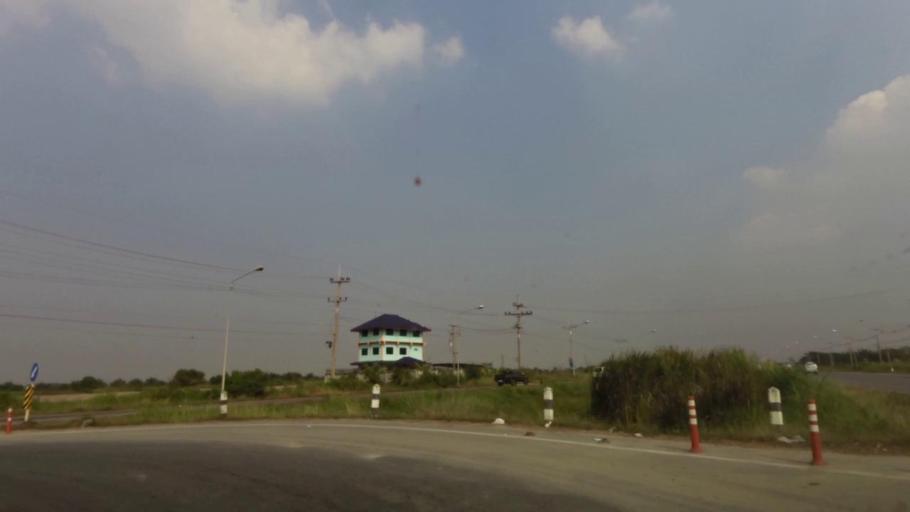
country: TH
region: Phra Nakhon Si Ayutthaya
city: Phra Nakhon Si Ayutthaya
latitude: 14.3043
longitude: 100.5739
